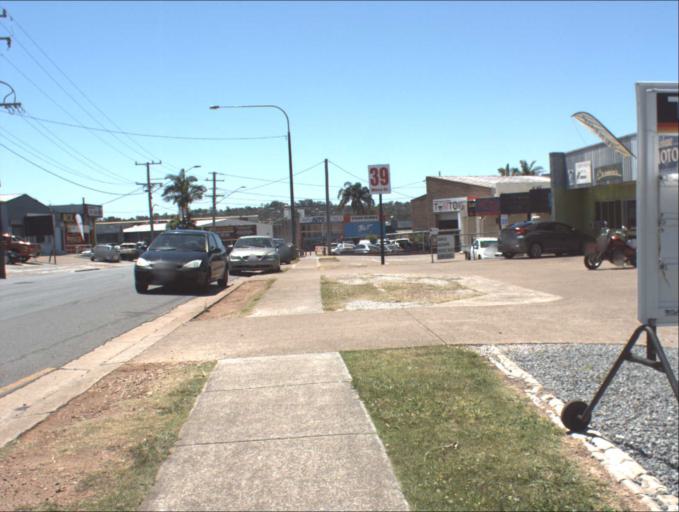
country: AU
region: Queensland
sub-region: Logan
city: Springwood
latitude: -27.6231
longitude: 153.1210
